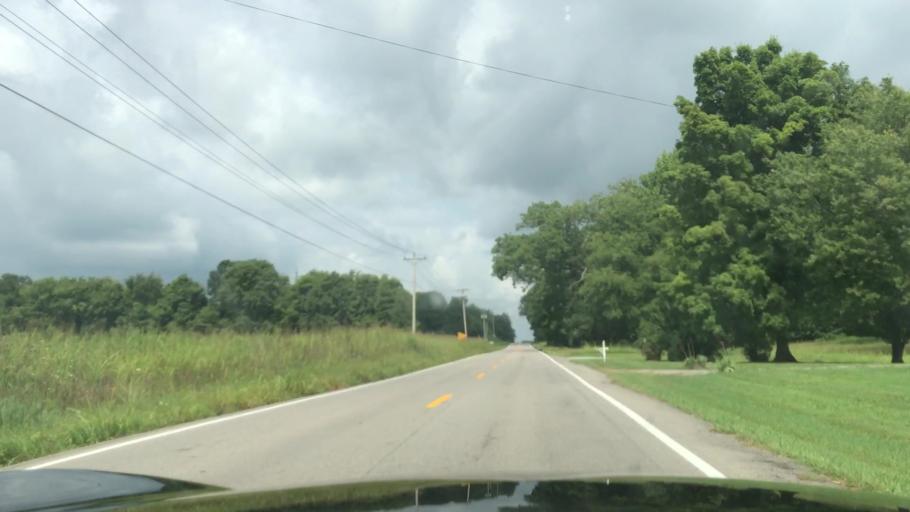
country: US
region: Kentucky
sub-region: Muhlenberg County
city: Central City
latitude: 37.1968
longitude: -86.9960
